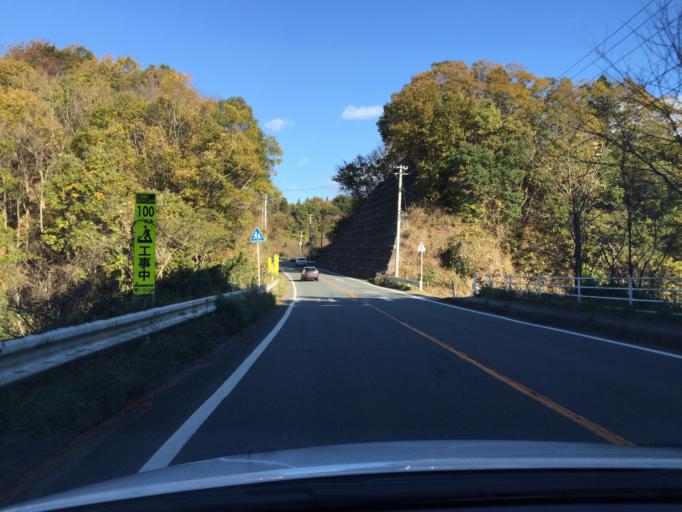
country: JP
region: Fukushima
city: Iwaki
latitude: 37.1544
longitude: 140.9963
